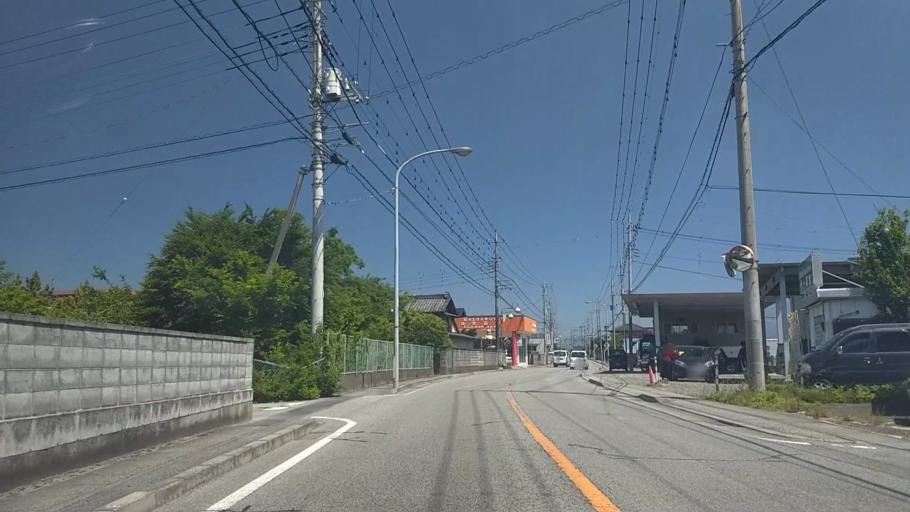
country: JP
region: Yamanashi
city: Ryuo
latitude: 35.6445
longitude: 138.4637
